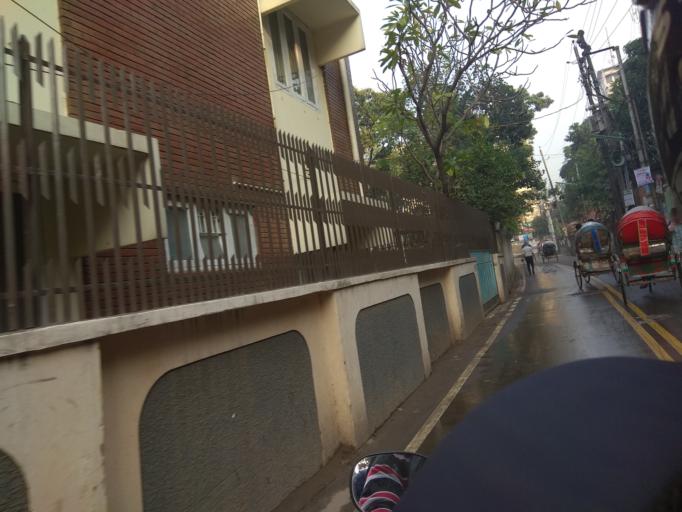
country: BD
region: Dhaka
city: Azimpur
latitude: 23.7570
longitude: 90.3819
